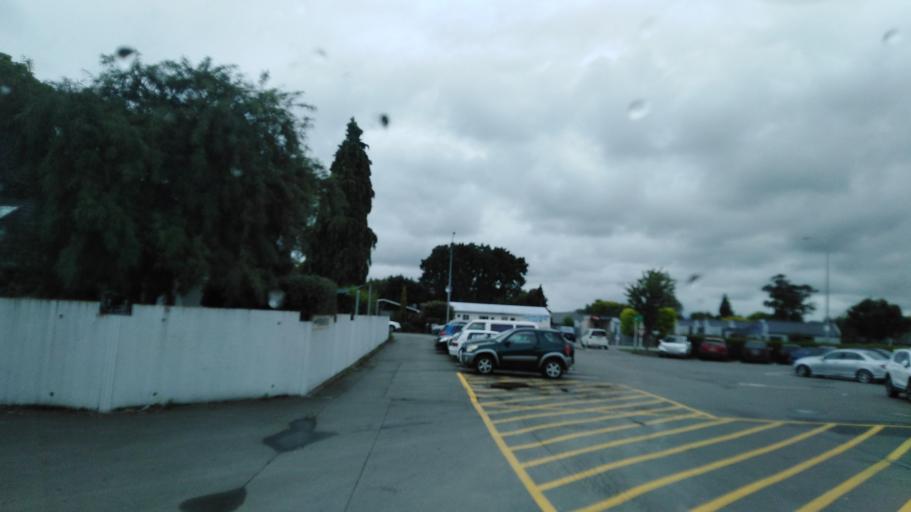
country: NZ
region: Marlborough
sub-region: Marlborough District
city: Blenheim
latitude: -41.5097
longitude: 173.9347
